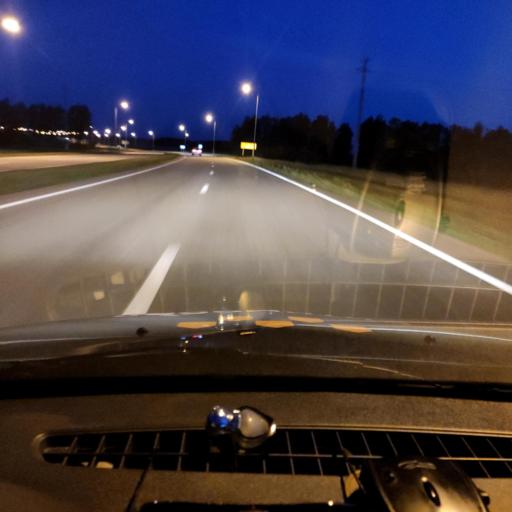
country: RU
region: Belgorod
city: Skorodnoye
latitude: 51.0752
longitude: 37.2069
